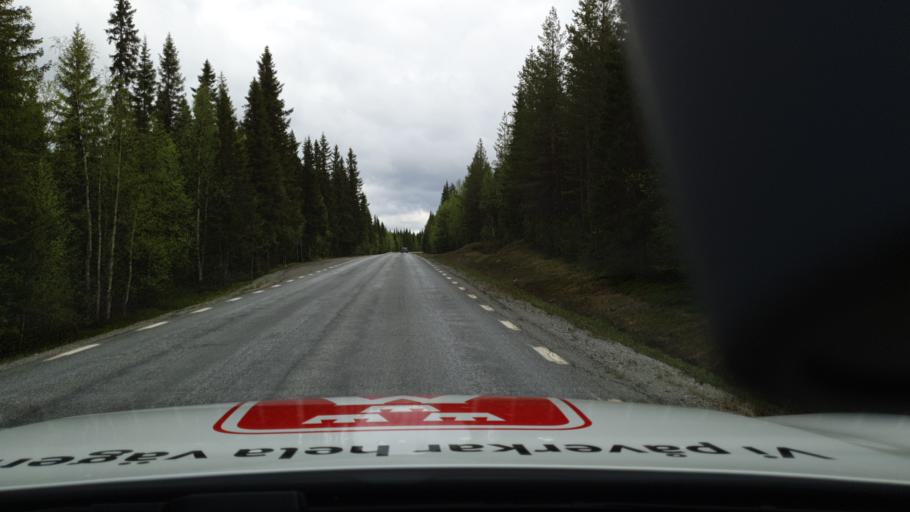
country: SE
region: Vaesterbotten
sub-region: Vilhelmina Kommun
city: Sjoberg
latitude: 64.7429
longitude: 16.1984
